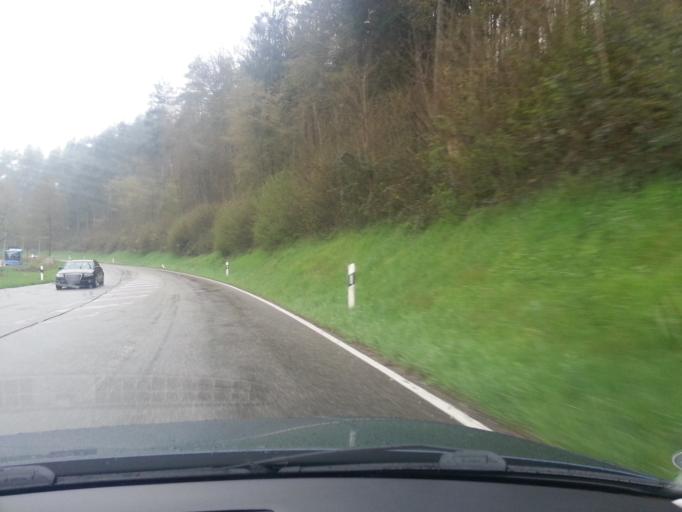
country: DE
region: Rheinland-Pfalz
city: Donsieders
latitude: 49.2678
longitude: 7.5923
